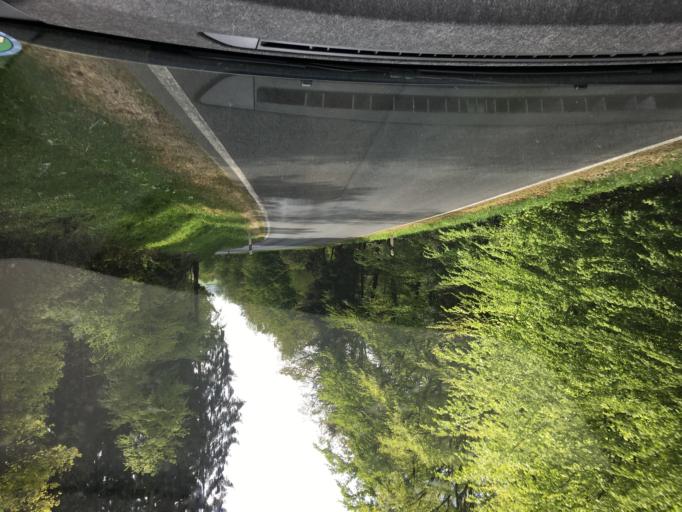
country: DE
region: Rheinland-Pfalz
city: Spessart
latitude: 50.4251
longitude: 7.1046
